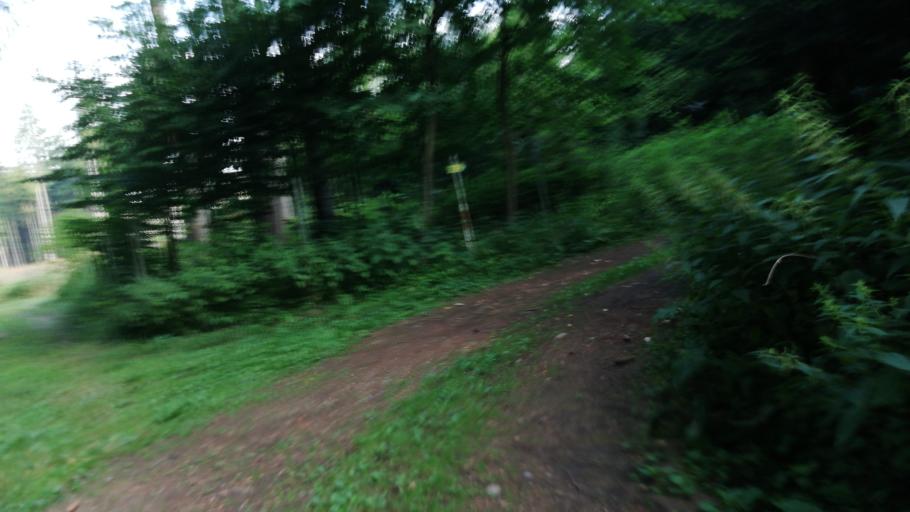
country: AT
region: Upper Austria
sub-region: Wels-Land
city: Buchkirchen
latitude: 48.1892
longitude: 13.9835
